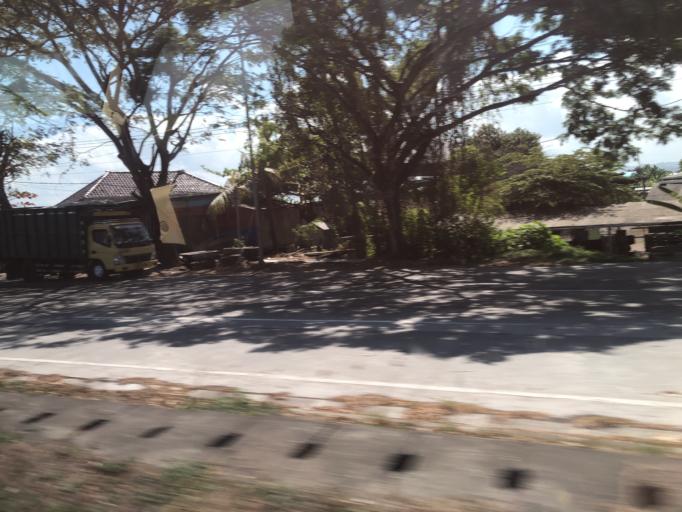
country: ID
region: Bali
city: Semarapura
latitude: -8.5659
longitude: 115.4154
